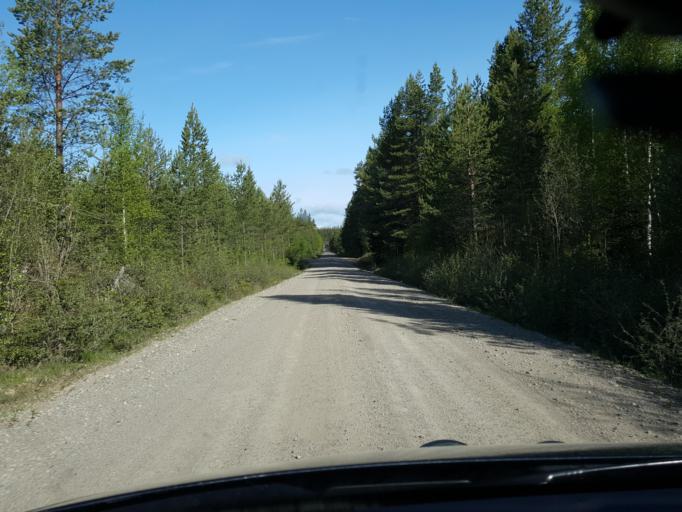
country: SE
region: Vaesternorrland
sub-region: Ange Kommun
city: Ange
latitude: 62.1865
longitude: 15.6030
